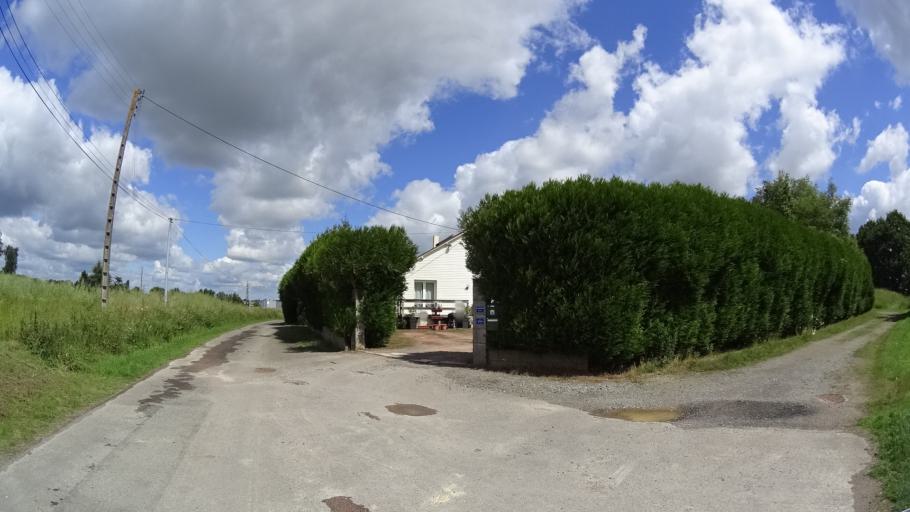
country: FR
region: Brittany
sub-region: Departement d'Ille-et-Vilaine
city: Le Rheu
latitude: 48.1161
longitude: -1.8268
